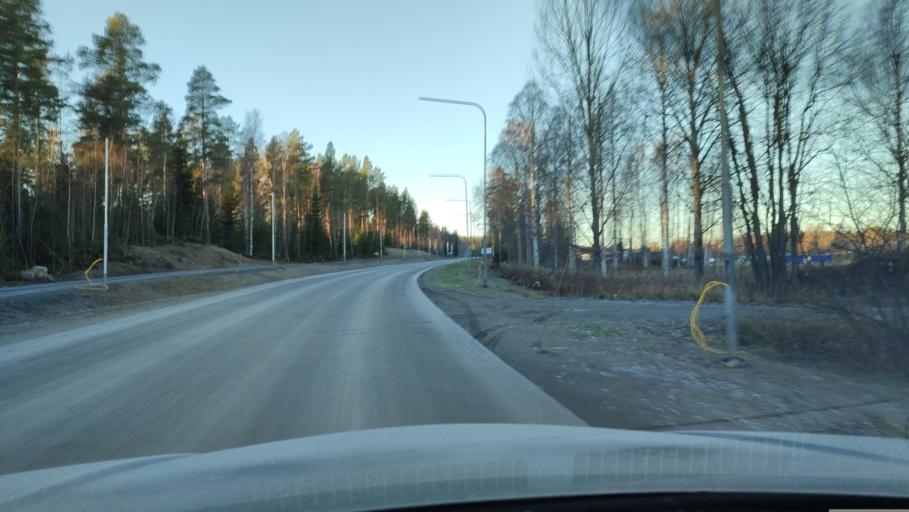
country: SE
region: Vaesterbotten
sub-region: Skelleftea Kommun
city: Skelleftea
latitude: 64.7397
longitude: 20.9405
